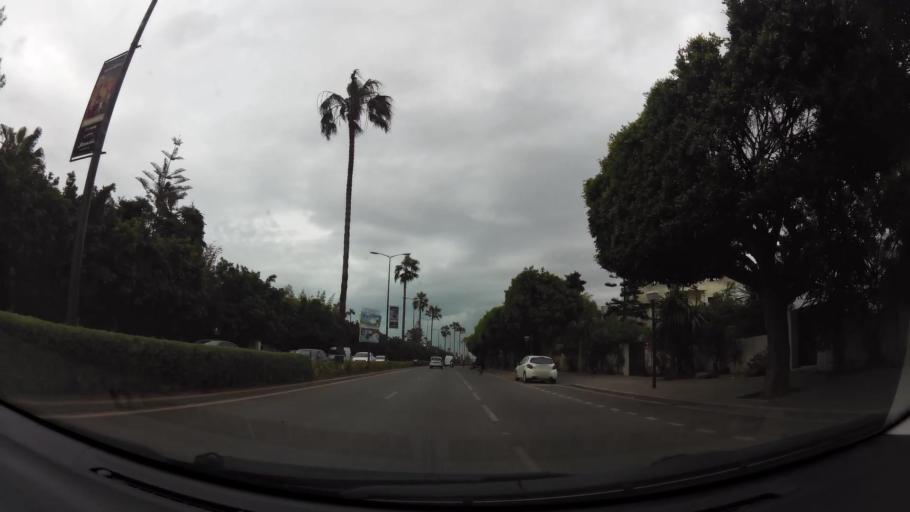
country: MA
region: Grand Casablanca
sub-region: Casablanca
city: Casablanca
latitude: 33.5796
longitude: -7.6680
